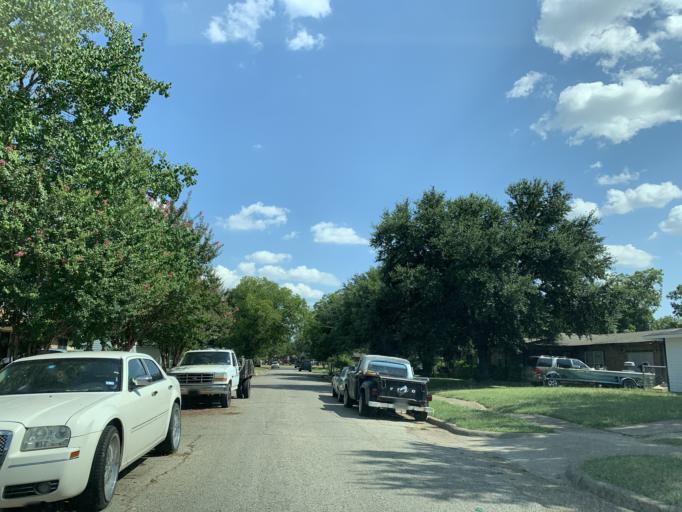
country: US
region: Texas
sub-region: Dallas County
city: Hutchins
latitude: 32.7011
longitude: -96.7720
